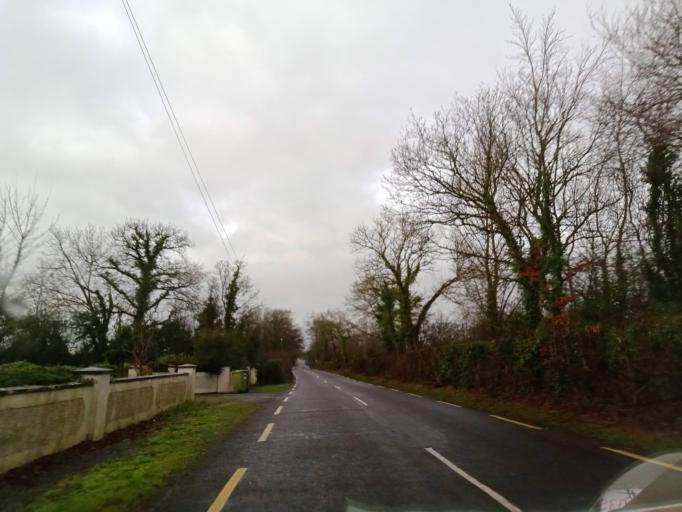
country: IE
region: Leinster
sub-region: Kilkenny
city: Callan
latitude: 52.5763
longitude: -7.3698
